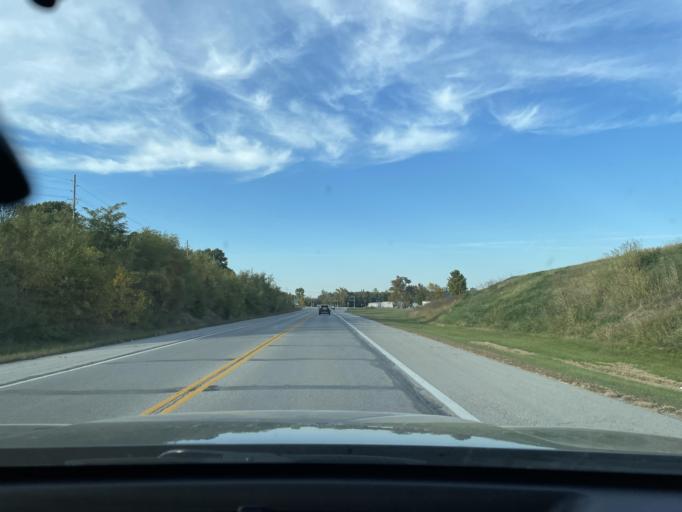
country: US
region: Missouri
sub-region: Andrew County
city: Country Club Village
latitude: 39.7789
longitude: -94.7675
